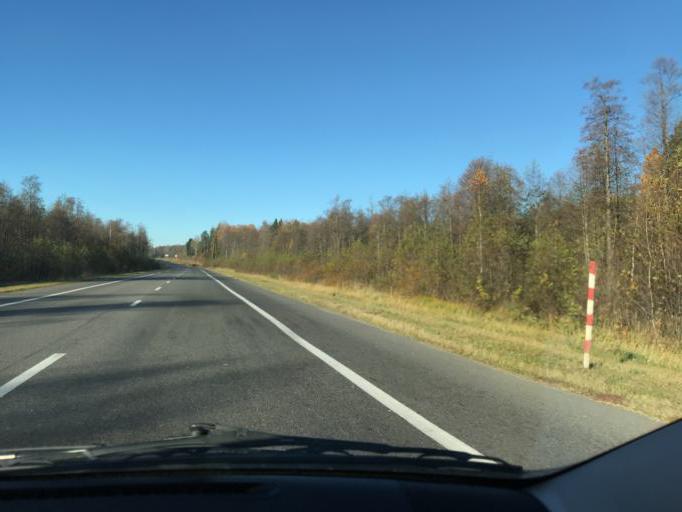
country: BY
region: Vitebsk
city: Vitebsk
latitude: 55.1032
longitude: 30.1813
